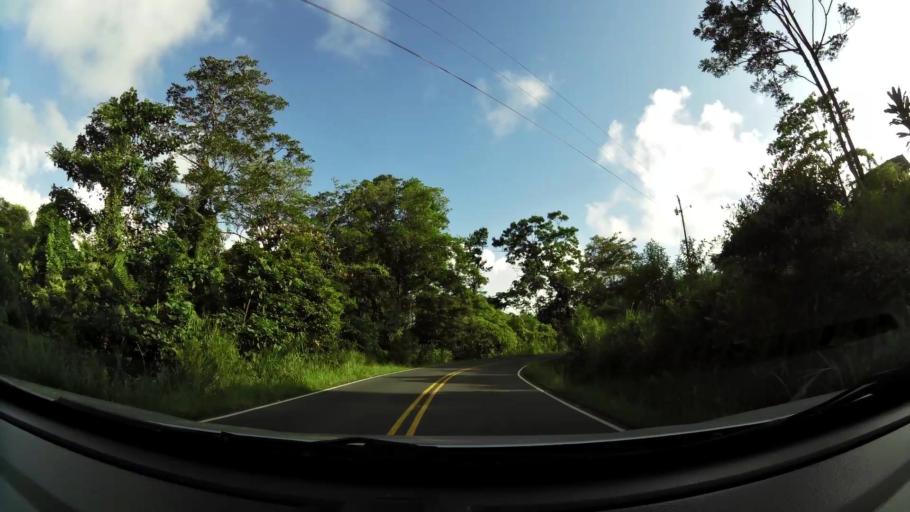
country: CR
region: Limon
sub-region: Canton de Siquirres
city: Siquirres
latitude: 10.0605
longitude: -83.5536
